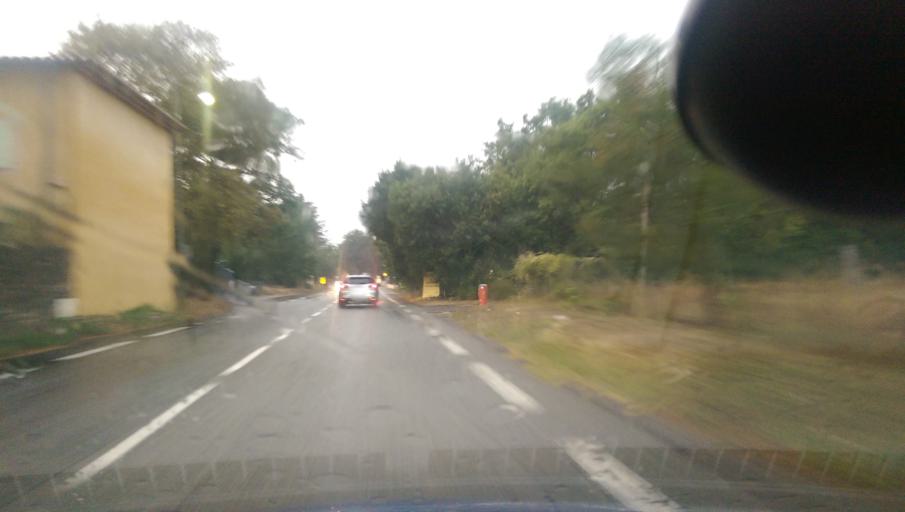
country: FR
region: Provence-Alpes-Cote d'Azur
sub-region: Departement des Alpes-Maritimes
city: Saint-Vallier-de-Thiey
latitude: 43.6905
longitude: 6.8664
